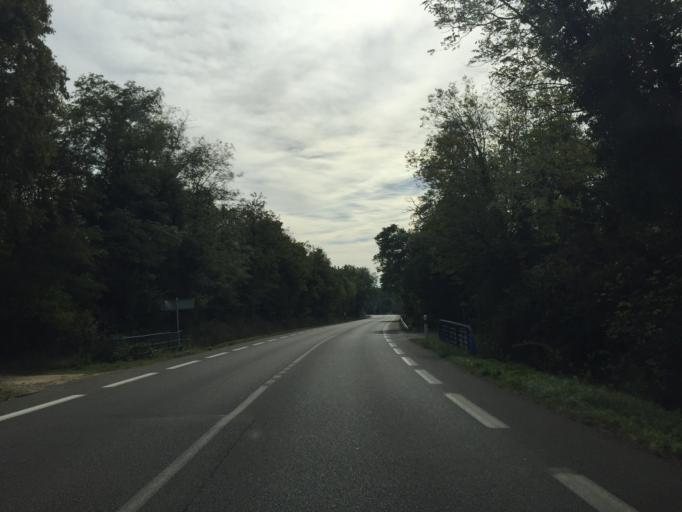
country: FR
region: Provence-Alpes-Cote d'Azur
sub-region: Departement du Vaucluse
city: Bollene
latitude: 44.2699
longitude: 4.7427
